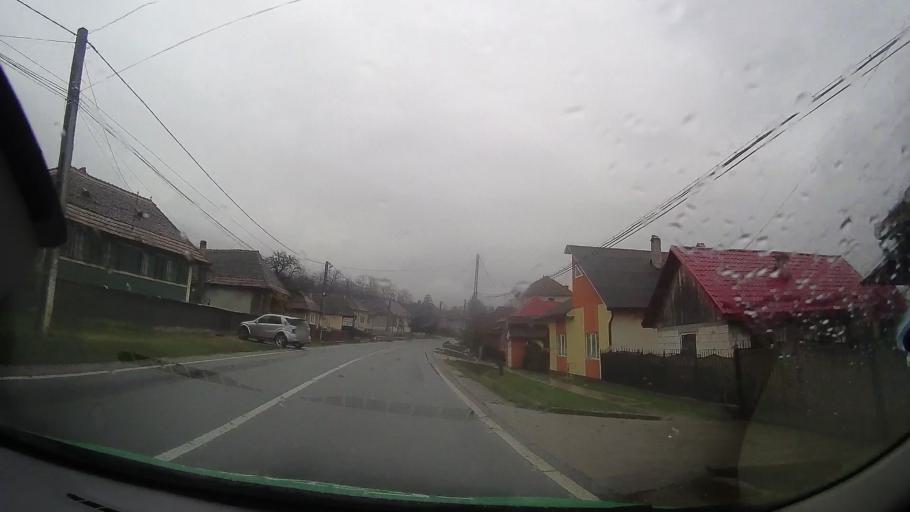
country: RO
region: Bistrita-Nasaud
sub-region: Comuna Galatii Bistritei
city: Galatii Bistritei
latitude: 46.9940
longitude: 24.4195
